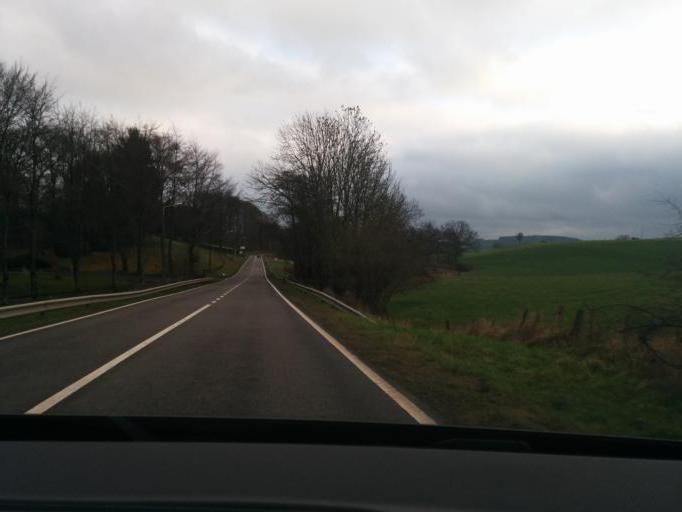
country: BE
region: Wallonia
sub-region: Province du Luxembourg
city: Gouvy
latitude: 50.1911
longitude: 5.9263
